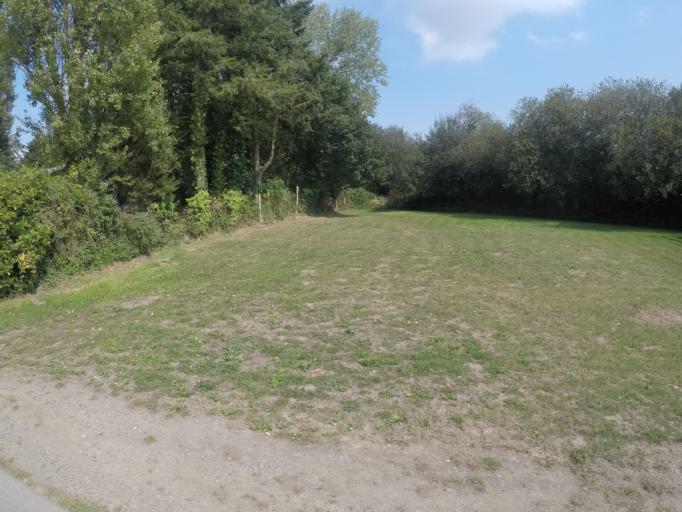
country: FR
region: Brittany
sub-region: Departement des Cotes-d'Armor
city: Saint-Donan
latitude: 48.5012
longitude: -2.9131
